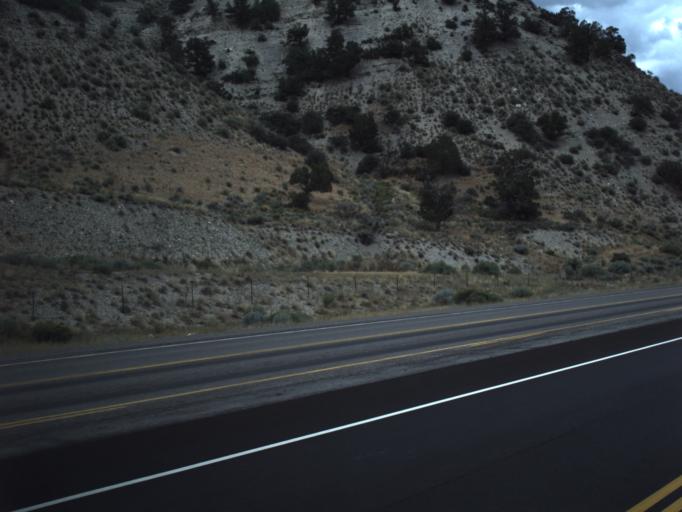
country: US
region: Utah
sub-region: Utah County
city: Mapleton
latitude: 39.9542
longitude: -111.2954
